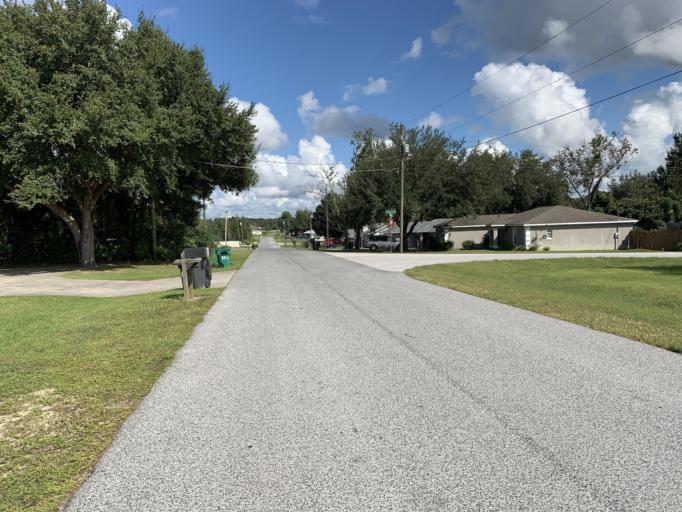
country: US
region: Florida
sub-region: Marion County
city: Silver Springs Shores
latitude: 29.1625
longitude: -82.0519
